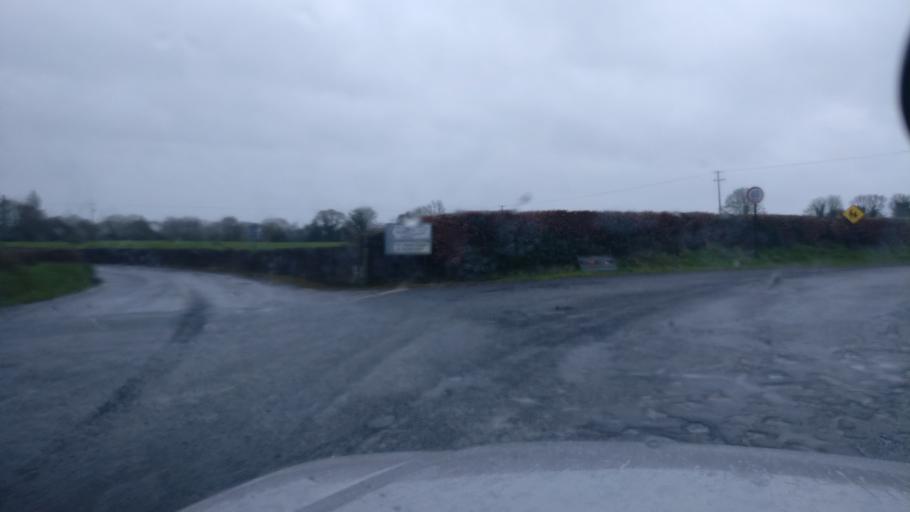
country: IE
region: Connaught
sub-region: County Galway
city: Ballinasloe
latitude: 53.2414
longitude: -8.1704
